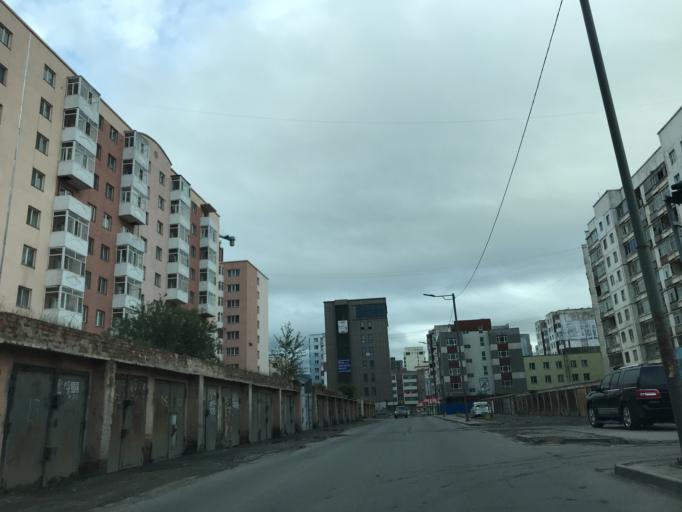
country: MN
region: Ulaanbaatar
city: Ulaanbaatar
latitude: 47.9143
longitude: 106.9395
